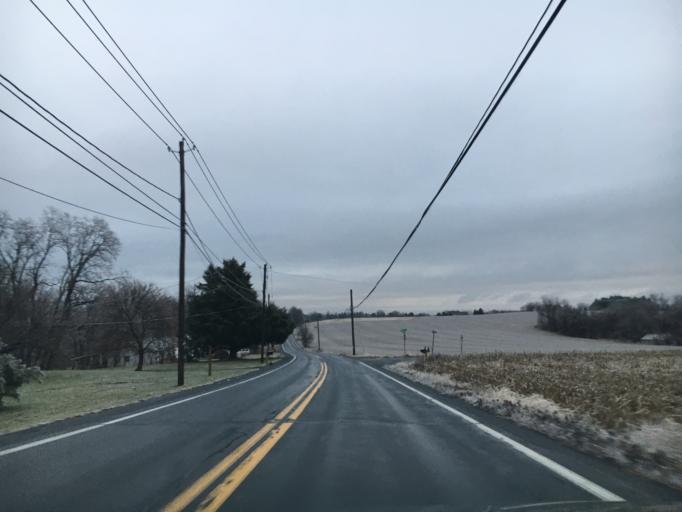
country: US
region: Pennsylvania
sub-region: Lehigh County
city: Schnecksville
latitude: 40.6222
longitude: -75.6298
